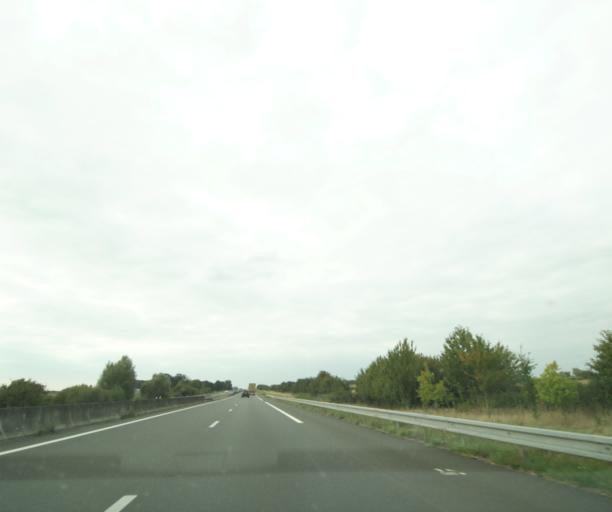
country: FR
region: Centre
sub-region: Departement d'Indre-et-Loire
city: Saint-Paterne-Racan
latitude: 47.6110
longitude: 0.5270
